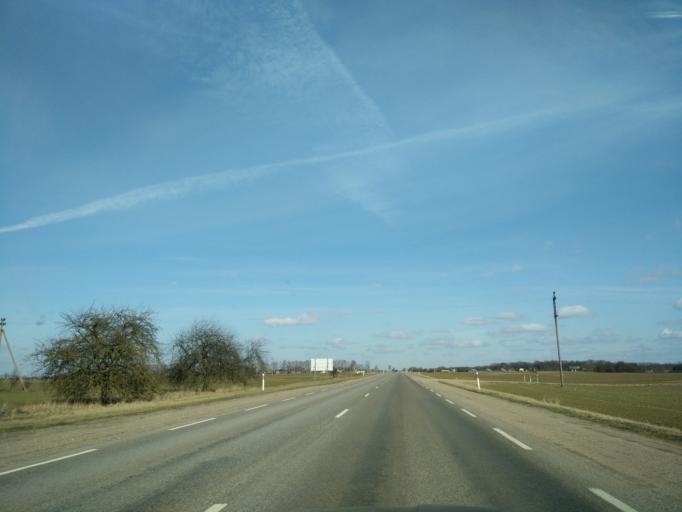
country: LT
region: Taurages apskritis
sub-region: Jurbarkas
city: Jurbarkas
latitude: 55.0833
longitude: 22.7934
